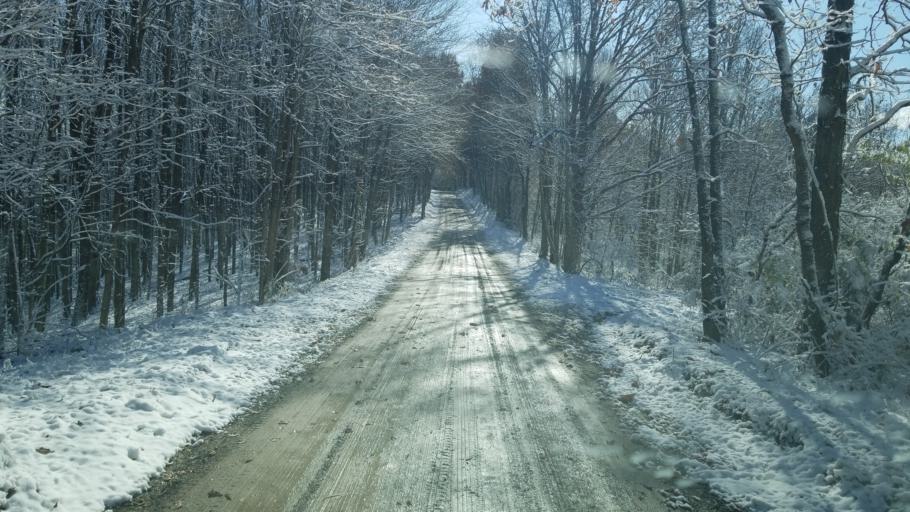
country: US
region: Ohio
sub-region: Licking County
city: Newark
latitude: 40.1502
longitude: -82.3496
